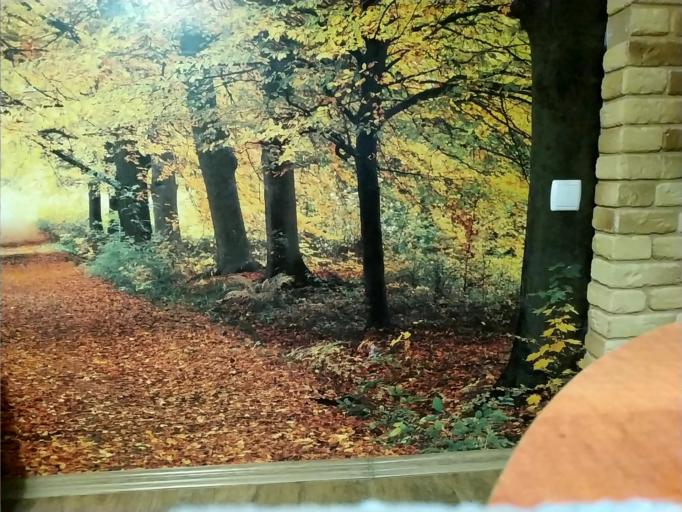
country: BY
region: Minsk
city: Plyeshchanitsy
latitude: 54.4274
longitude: 27.6078
